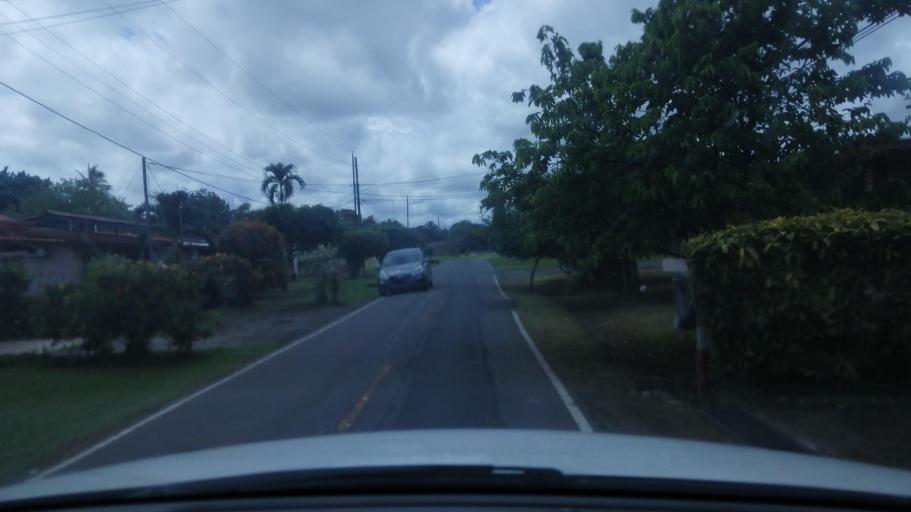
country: PA
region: Chiriqui
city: David
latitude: 8.4161
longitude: -82.4286
